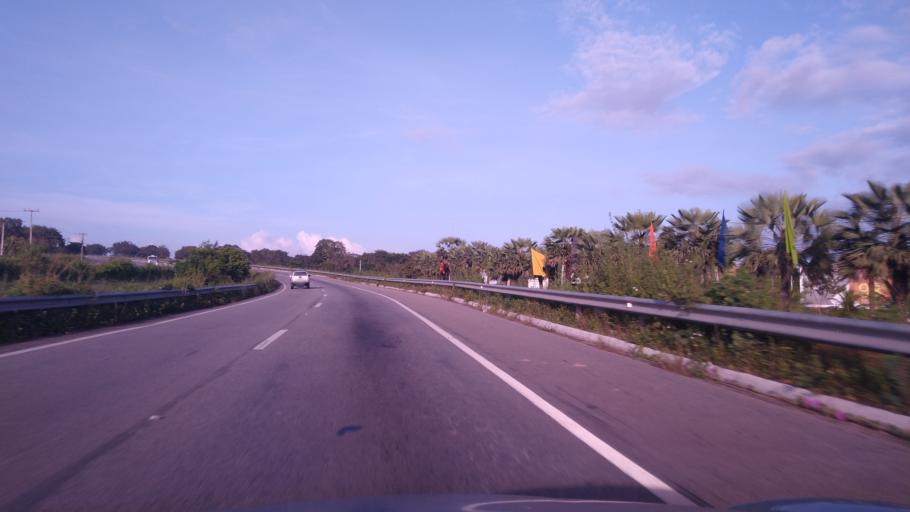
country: BR
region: Ceara
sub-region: Pacajus
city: Pacajus
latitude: -4.1661
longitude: -38.4910
